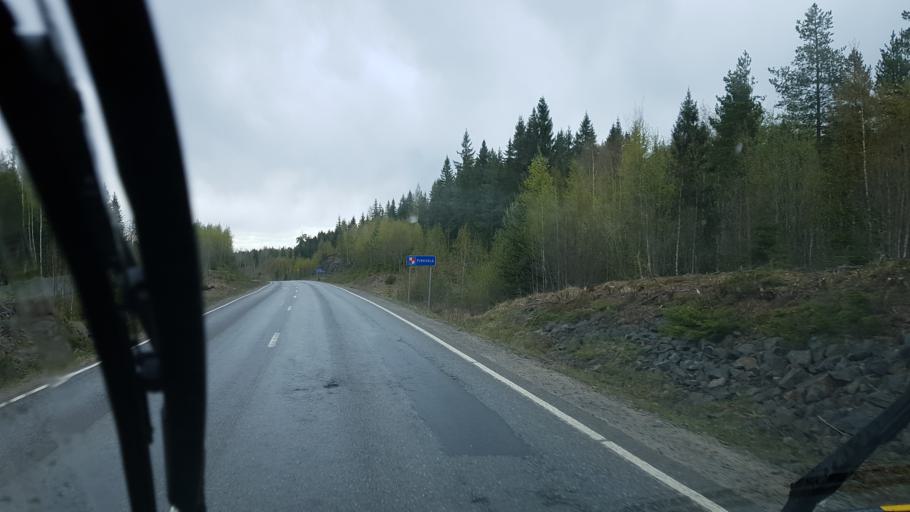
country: FI
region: Pirkanmaa
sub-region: Tampere
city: Pirkkala
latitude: 61.4052
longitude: 23.6325
